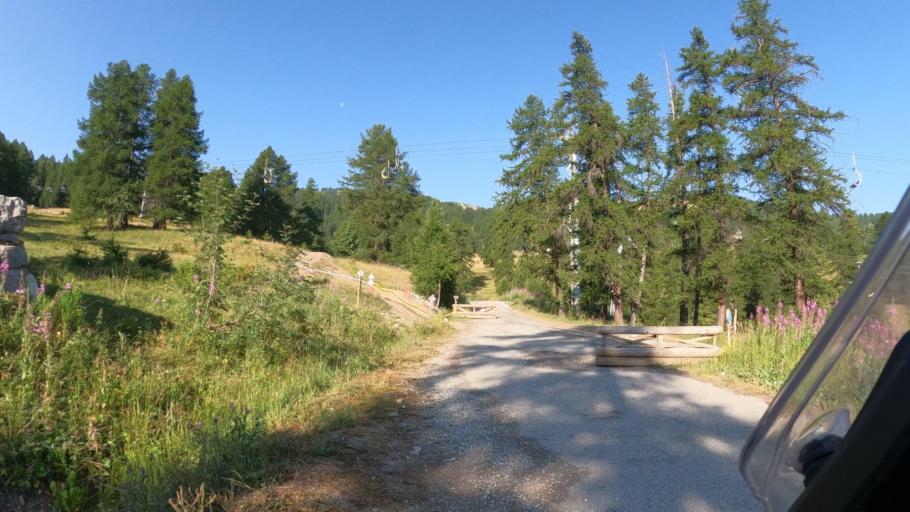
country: FR
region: Provence-Alpes-Cote d'Azur
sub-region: Departement des Hautes-Alpes
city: Guillestre
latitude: 44.6187
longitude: 6.6337
